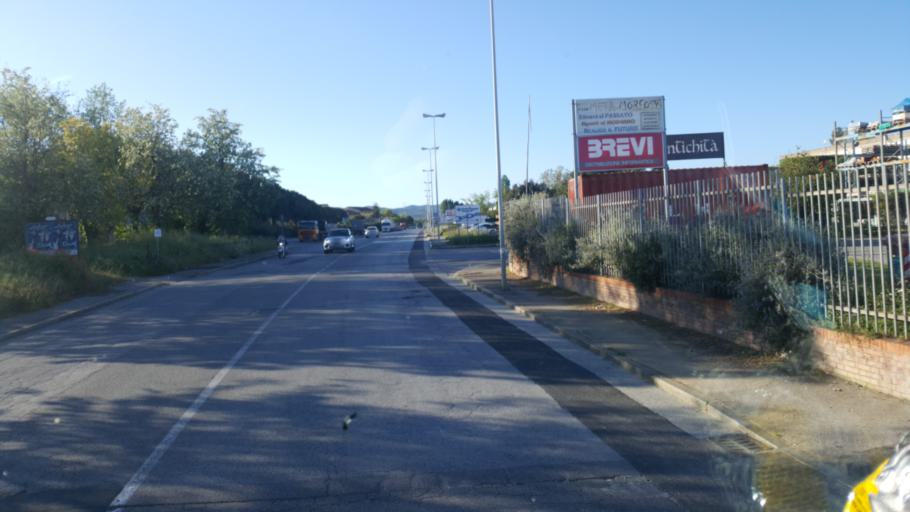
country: IT
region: Tuscany
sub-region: Provincia di Livorno
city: Livorno
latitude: 43.5720
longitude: 10.3380
